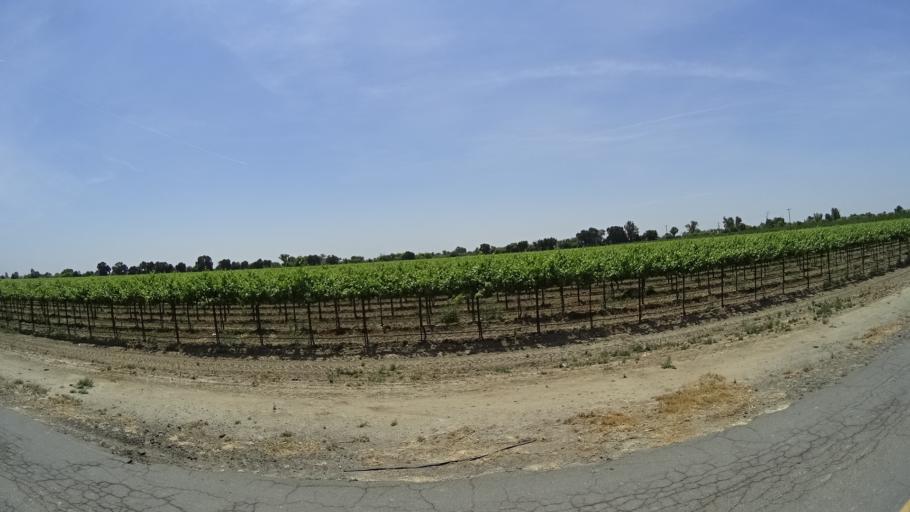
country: US
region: California
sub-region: Fresno County
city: Riverdale
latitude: 36.3875
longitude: -119.8630
